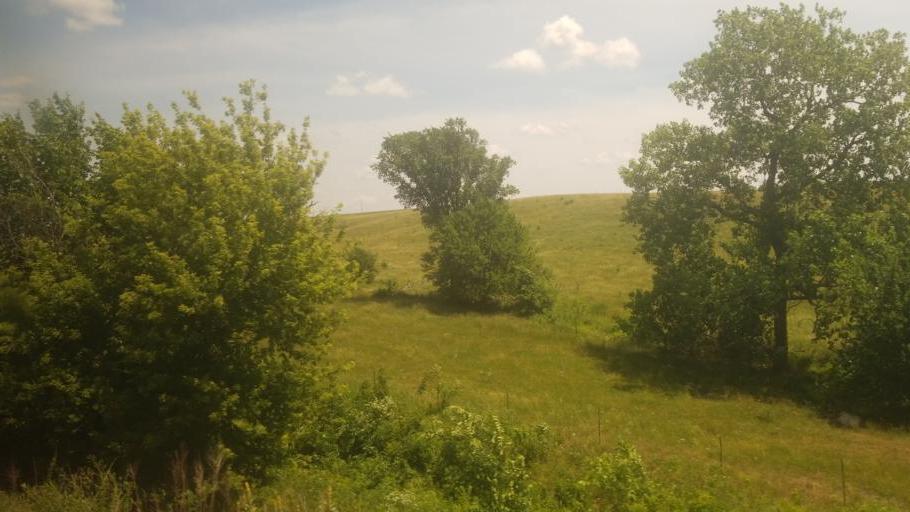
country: US
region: Missouri
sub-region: Linn County
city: Marceline
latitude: 39.8537
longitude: -92.8101
